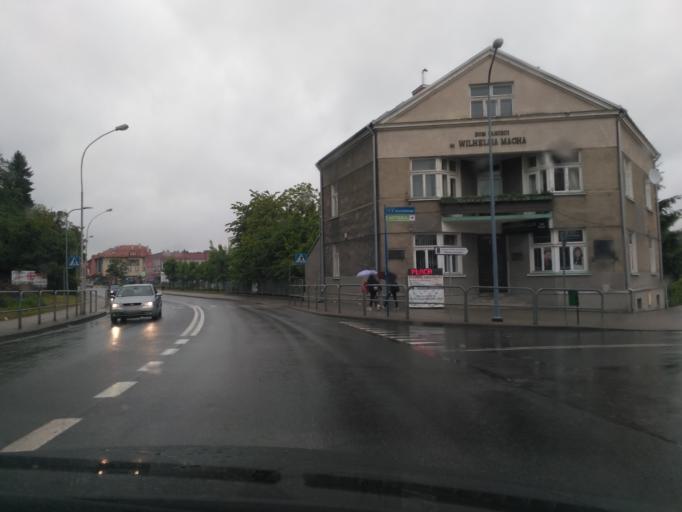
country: PL
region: Lesser Poland Voivodeship
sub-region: Powiat gorlicki
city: Gorlice
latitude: 49.6579
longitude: 21.1596
